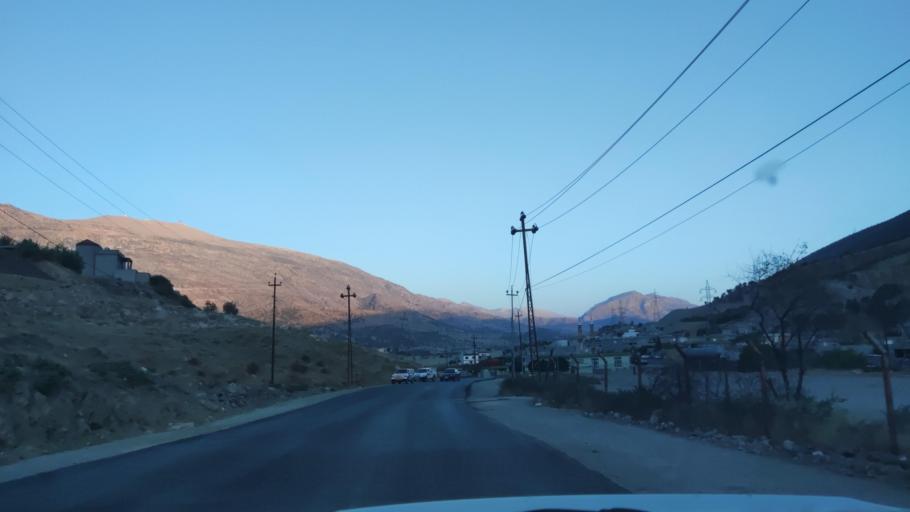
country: IQ
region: Arbil
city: Ruwandiz
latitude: 36.5929
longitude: 44.3846
